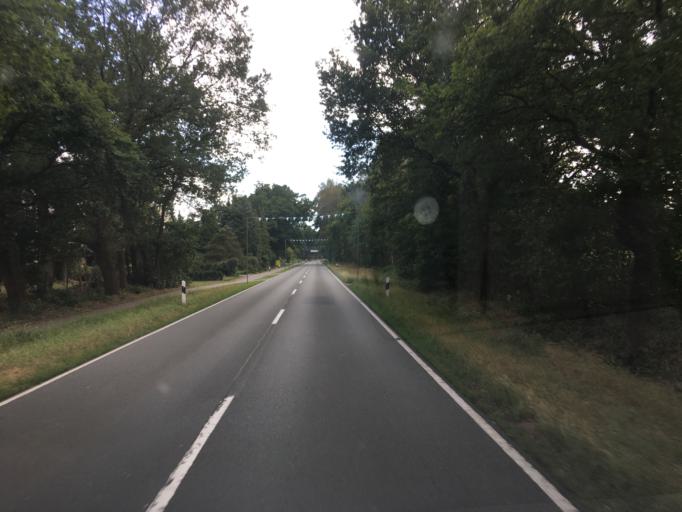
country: DE
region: Lower Saxony
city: Friesoythe
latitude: 53.0719
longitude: 7.8461
